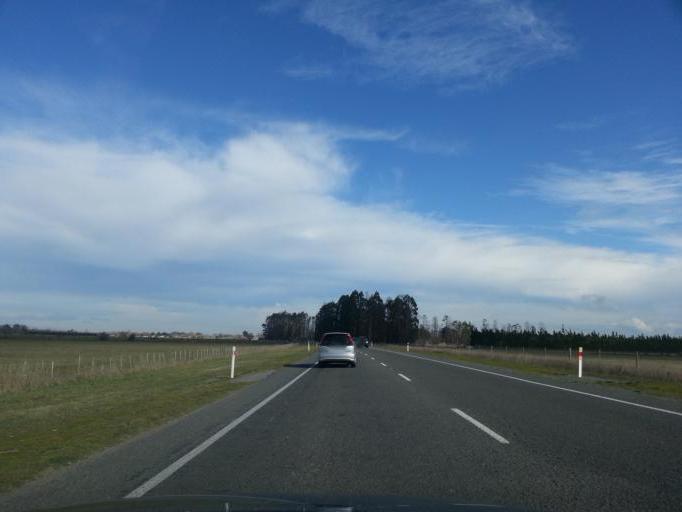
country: NZ
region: Canterbury
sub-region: Waimakariri District
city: Kaiapoi
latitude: -43.3587
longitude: 172.6550
